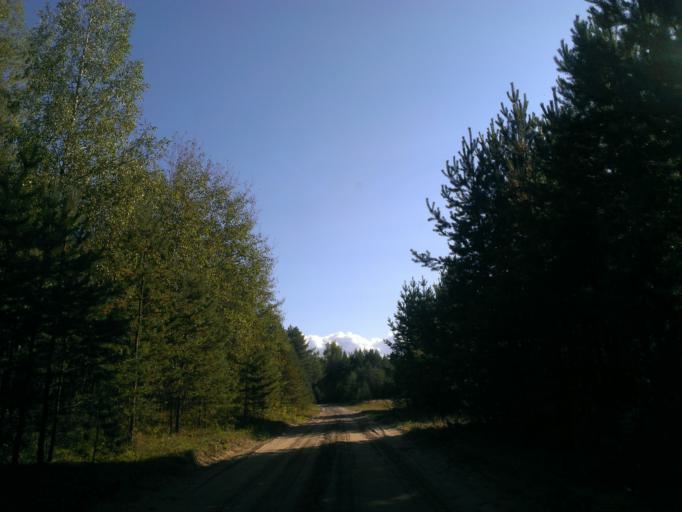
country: LV
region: Adazi
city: Adazi
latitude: 57.0551
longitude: 24.2560
